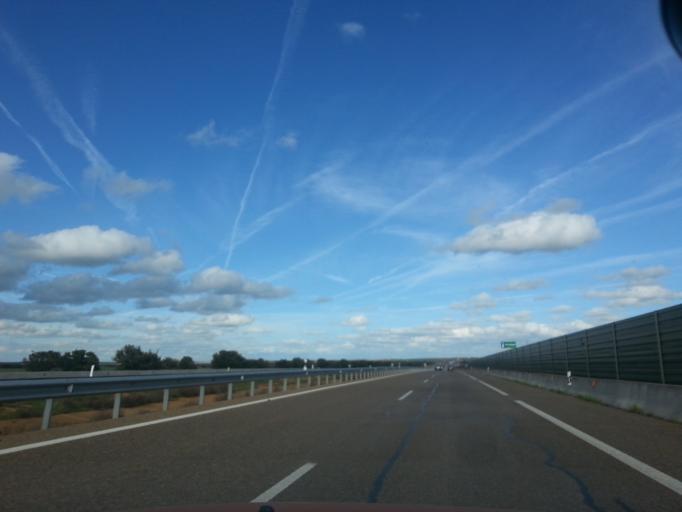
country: ES
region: Castille and Leon
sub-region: Provincia de Salamanca
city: Galindo y Perahuy
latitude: 40.9290
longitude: -5.8213
